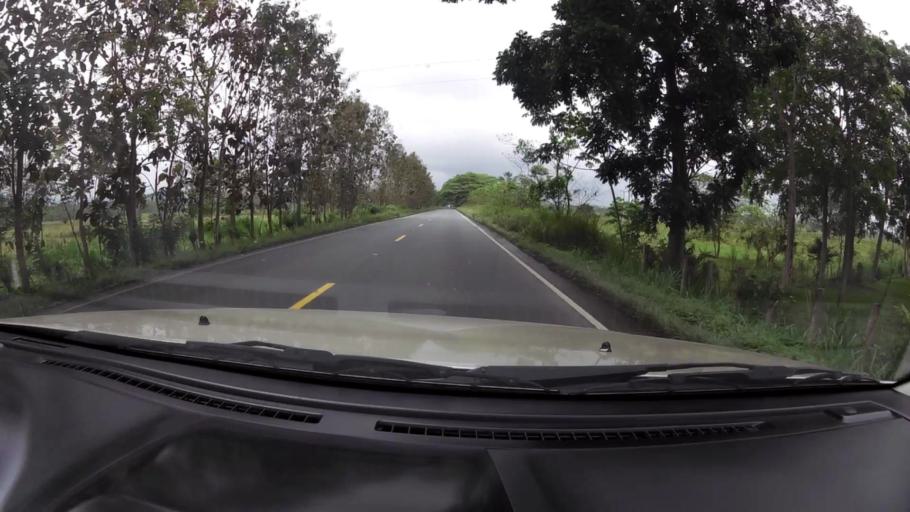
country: EC
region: Guayas
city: Balao
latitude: -2.9657
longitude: -79.7220
